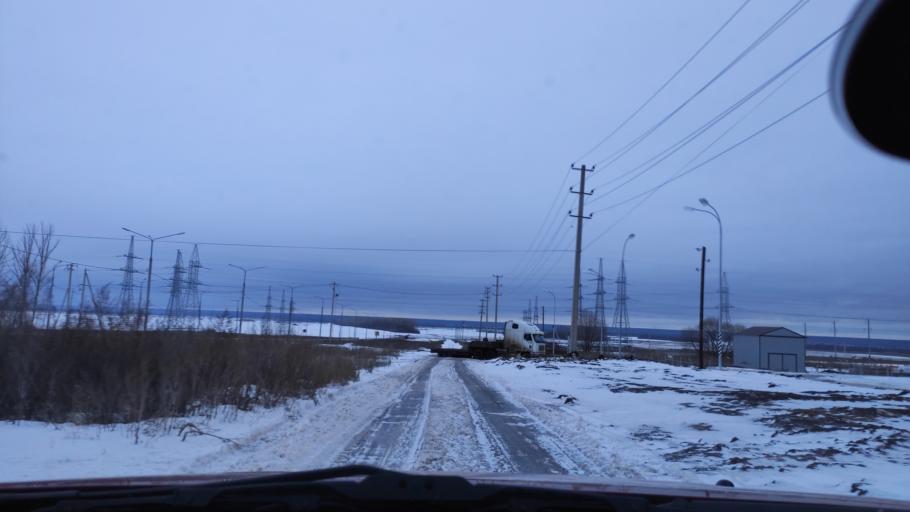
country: RU
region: Tambov
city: Donskoye
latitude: 52.7862
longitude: 41.4262
